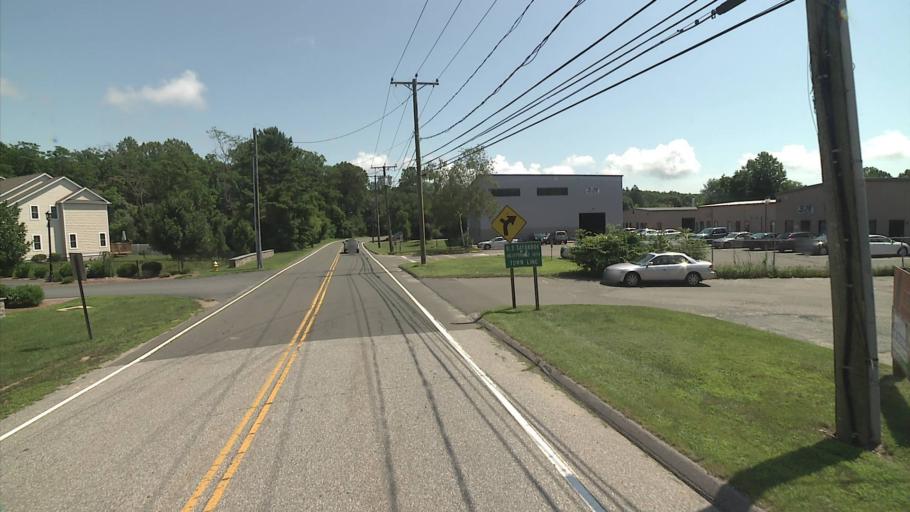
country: US
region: Connecticut
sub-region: Middlesex County
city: Westbrook Center
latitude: 41.2929
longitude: -72.4250
